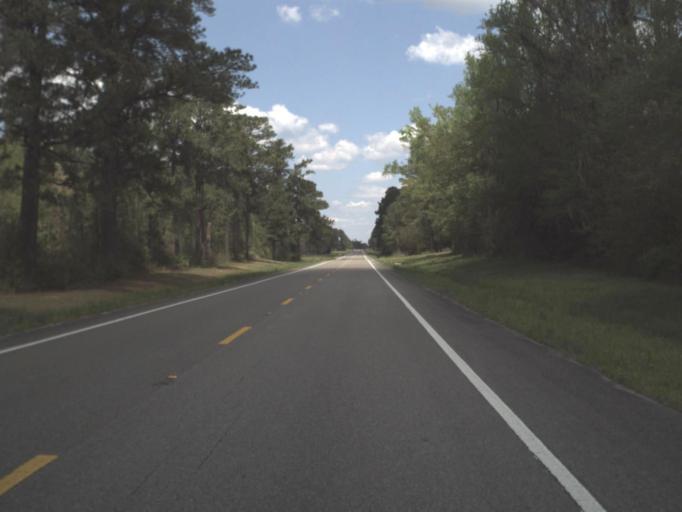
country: US
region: Florida
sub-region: Okaloosa County
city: Crestview
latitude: 30.9748
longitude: -86.6309
